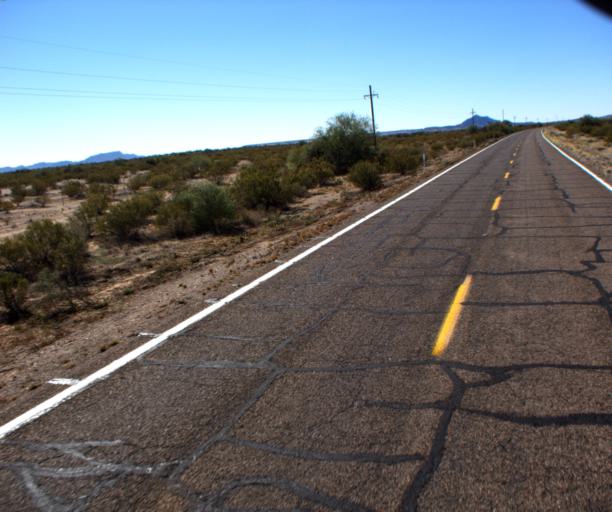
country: US
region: Arizona
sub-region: Pima County
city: Ajo
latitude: 32.4529
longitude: -112.8716
